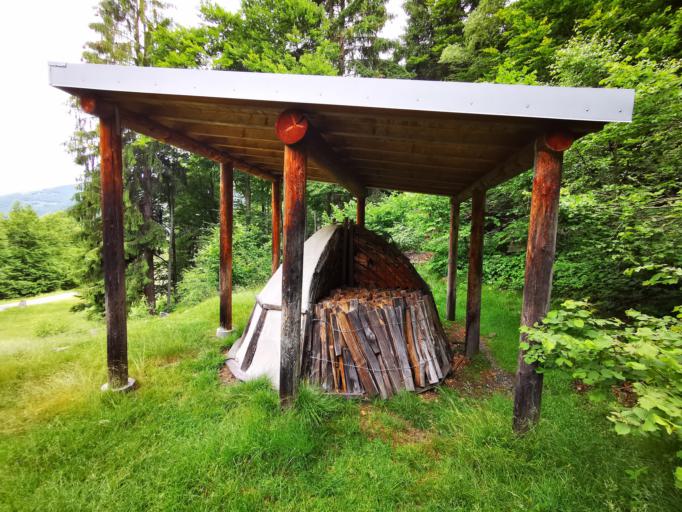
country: IT
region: Lombardy
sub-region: Provincia di Como
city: Cavargna
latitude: 46.1615
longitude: 9.1143
